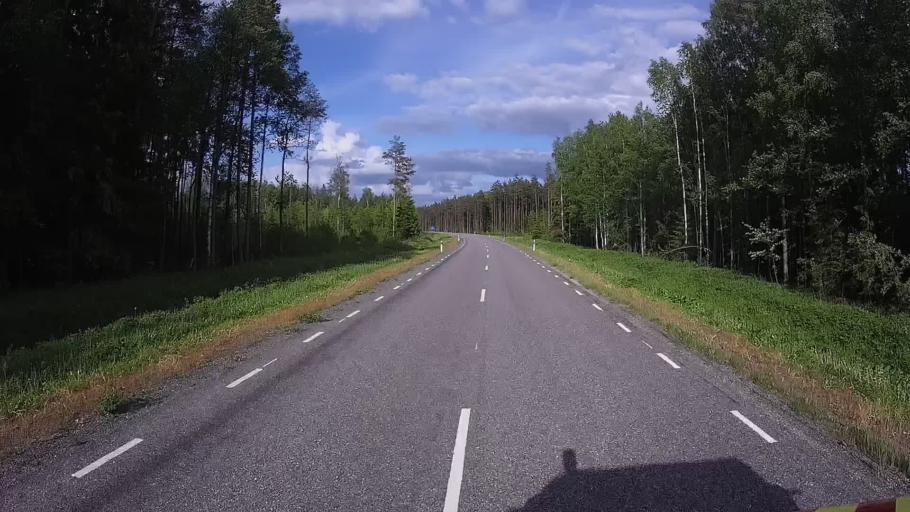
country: EE
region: Jogevamaa
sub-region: Mustvee linn
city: Mustvee
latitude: 59.0228
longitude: 27.0705
